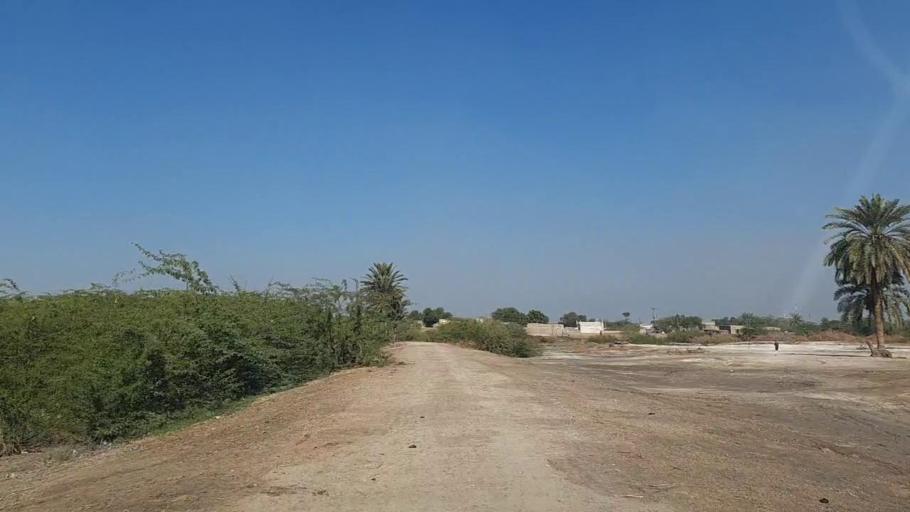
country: PK
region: Sindh
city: Nawabshah
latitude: 26.3402
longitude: 68.3544
